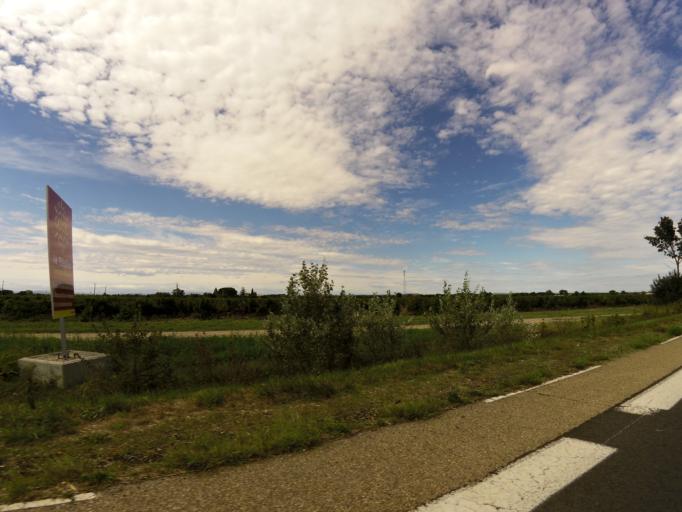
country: FR
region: Languedoc-Roussillon
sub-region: Departement du Gard
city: Aimargues
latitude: 43.6625
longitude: 4.2082
